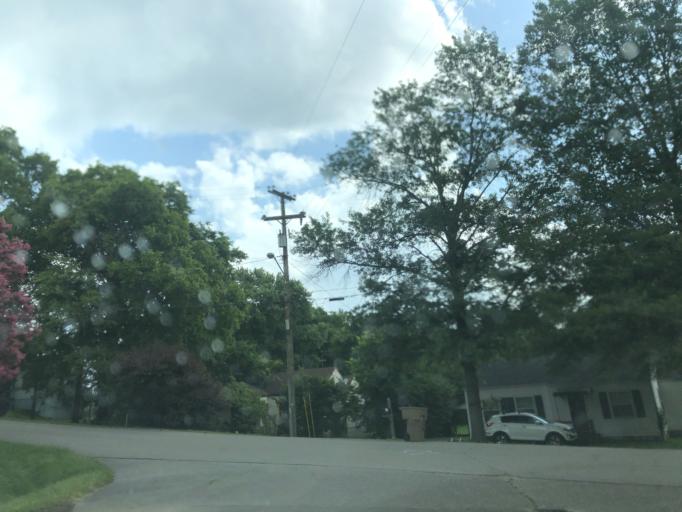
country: US
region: Tennessee
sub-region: Davidson County
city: Lakewood
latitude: 36.1603
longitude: -86.6589
